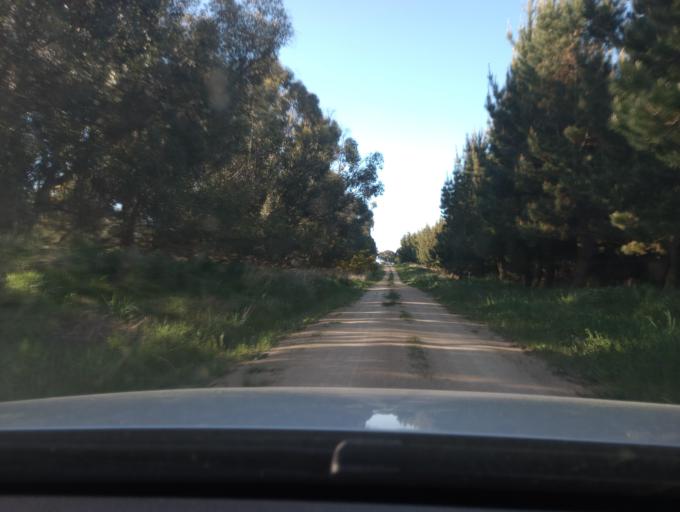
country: AU
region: New South Wales
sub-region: Blayney
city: Millthorpe
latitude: -33.4061
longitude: 149.3077
